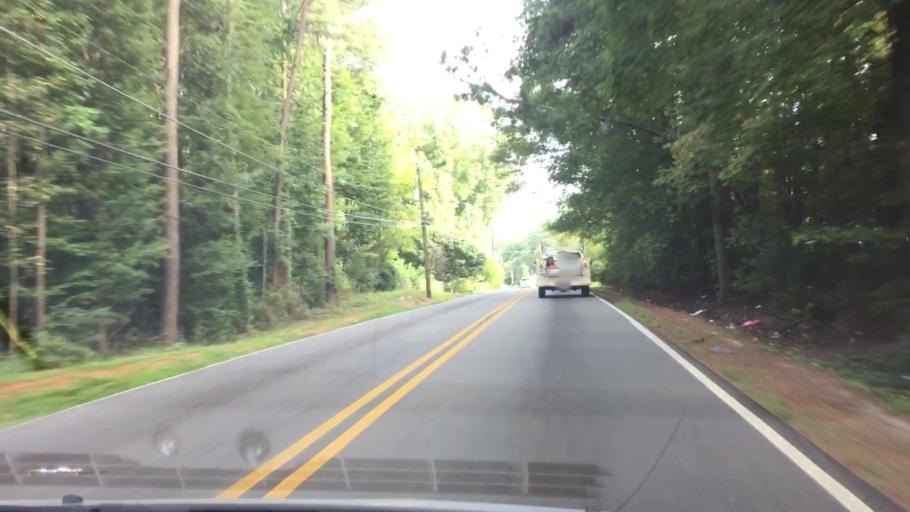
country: US
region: Georgia
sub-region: Clayton County
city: Conley
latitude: 33.6542
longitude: -84.2856
